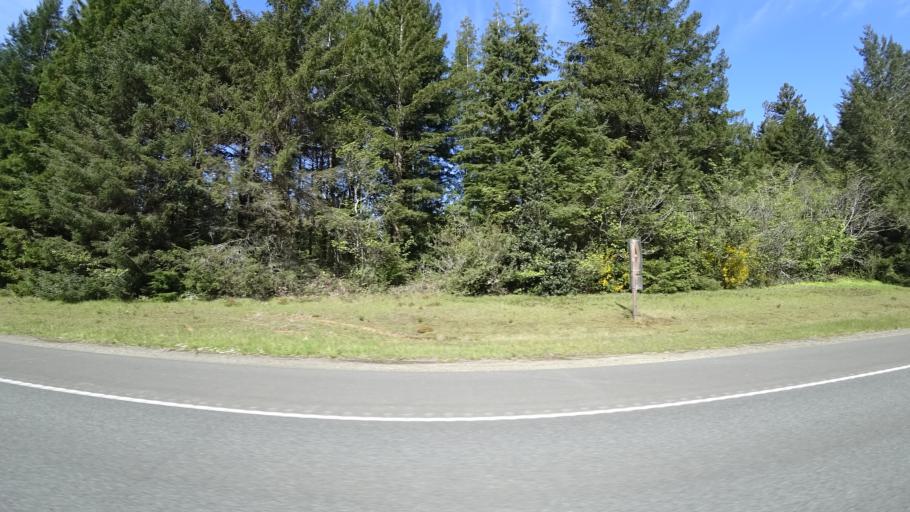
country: US
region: California
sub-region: Del Norte County
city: Bertsch-Oceanview
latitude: 41.8048
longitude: -124.1482
